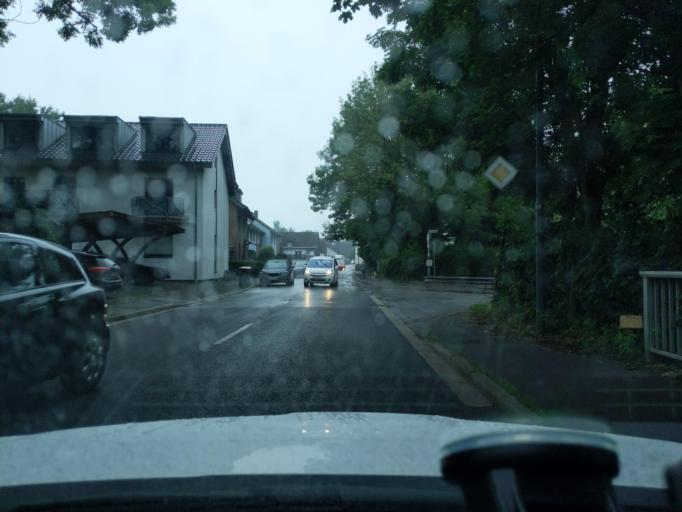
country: DE
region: North Rhine-Westphalia
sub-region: Regierungsbezirk Dusseldorf
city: Ratingen
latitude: 51.2834
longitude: 6.8579
